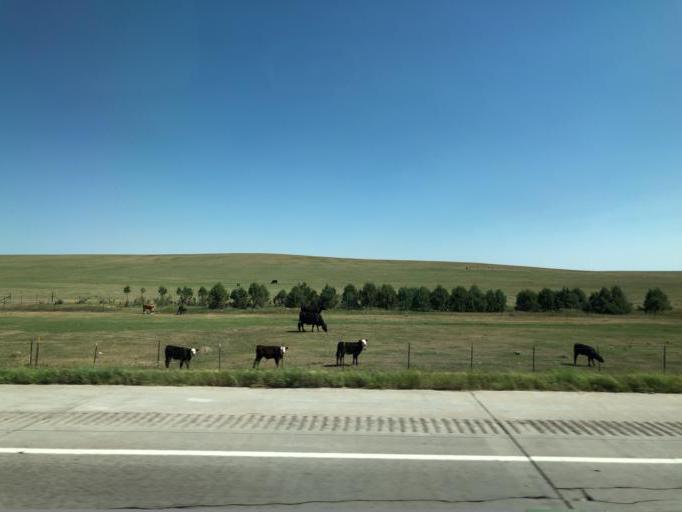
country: US
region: Colorado
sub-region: Lincoln County
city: Limon
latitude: 39.2770
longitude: -103.7511
